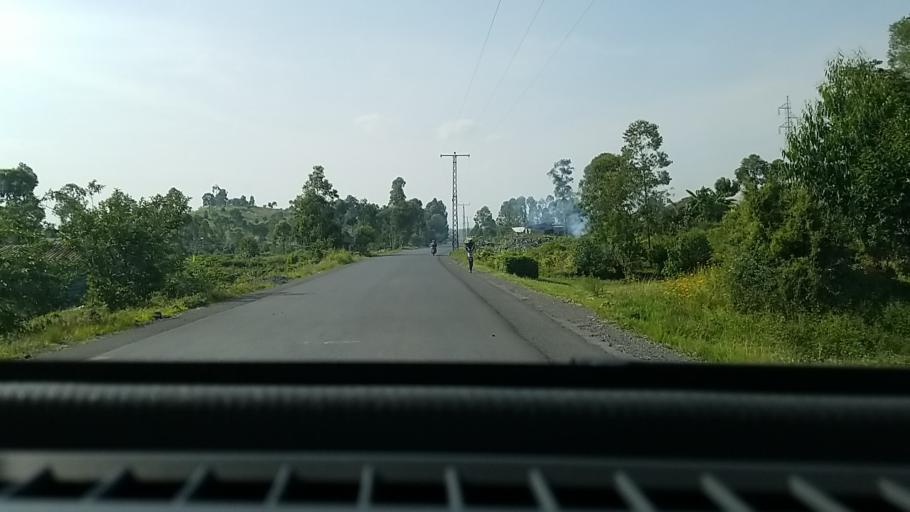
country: CD
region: Nord Kivu
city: Goma
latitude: -1.6147
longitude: 29.1431
